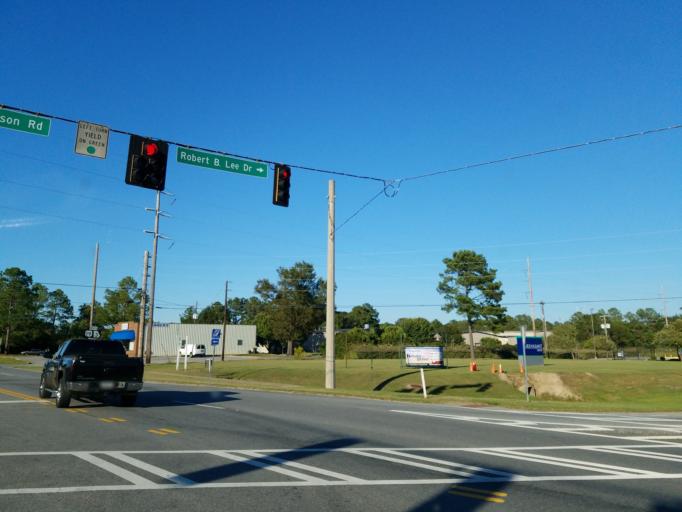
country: US
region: Georgia
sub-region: Lee County
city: Leesburg
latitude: 31.7201
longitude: -84.1723
